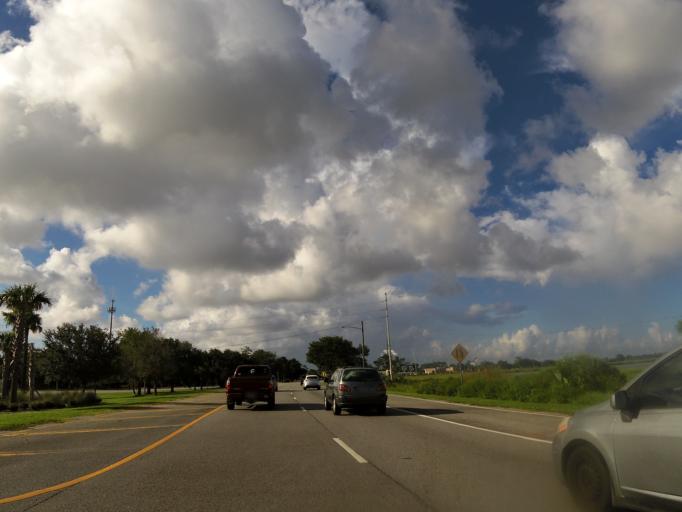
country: US
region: Georgia
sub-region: Glynn County
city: Brunswick
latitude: 31.1536
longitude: -81.4787
